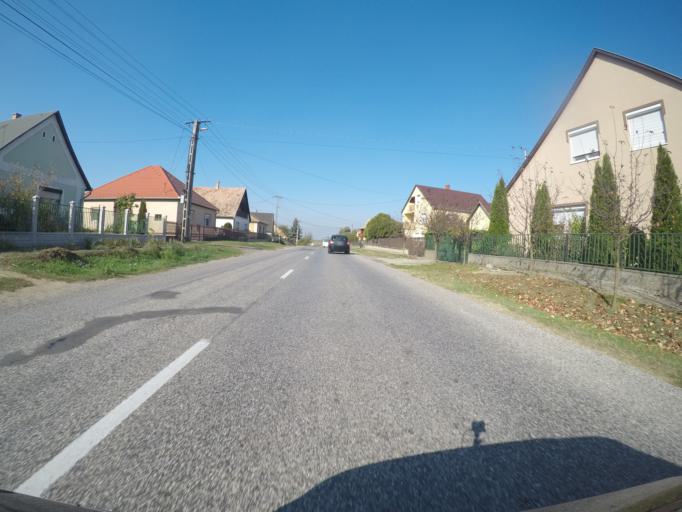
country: HU
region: Tolna
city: Szedres
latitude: 46.4868
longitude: 18.6803
